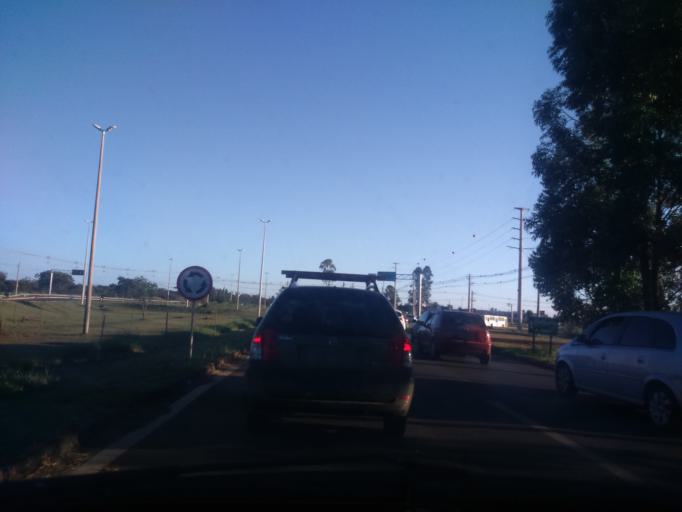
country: BR
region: Federal District
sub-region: Brasilia
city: Brasilia
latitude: -15.8868
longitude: -47.8215
